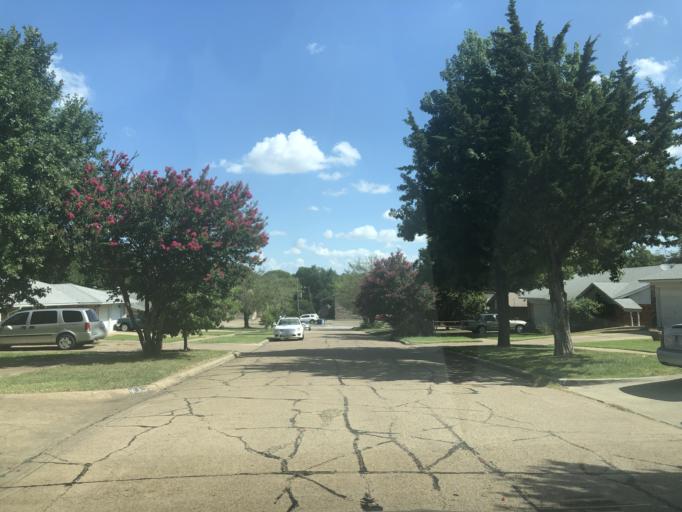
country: US
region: Texas
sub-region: Dallas County
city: Grand Prairie
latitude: 32.7341
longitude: -97.0014
